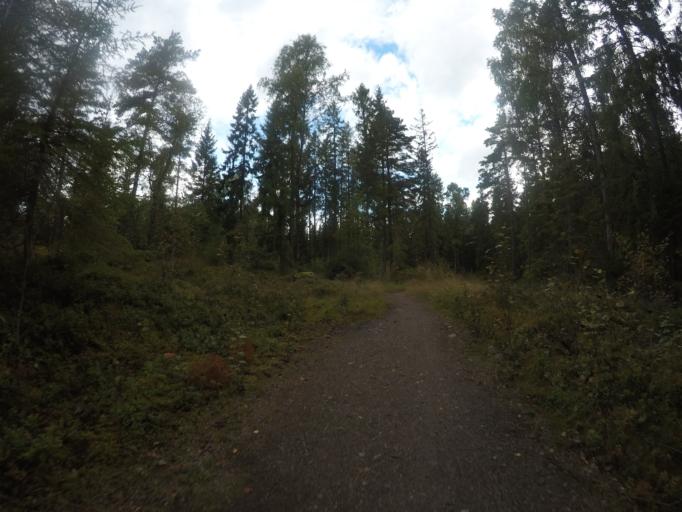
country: SE
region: Vaestmanland
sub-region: Vasteras
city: Vasteras
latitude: 59.6675
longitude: 16.5238
